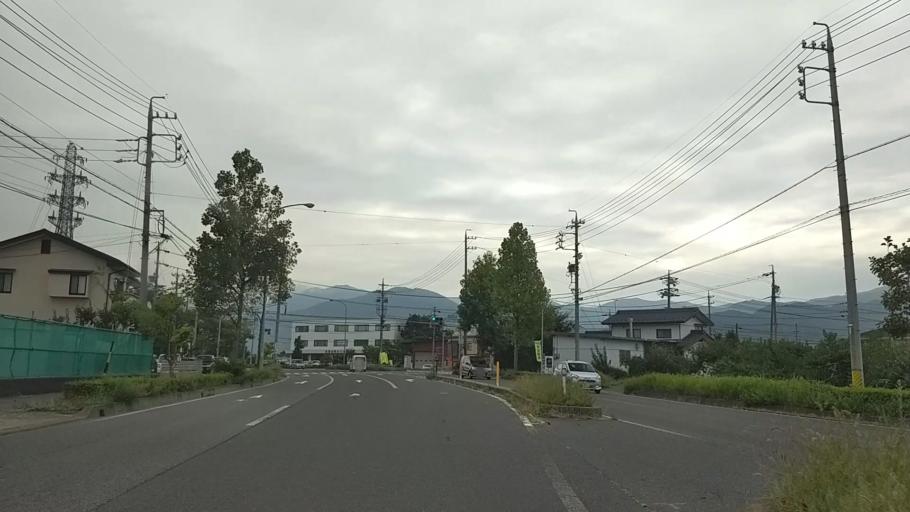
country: JP
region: Nagano
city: Nagano-shi
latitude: 36.6126
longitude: 138.2080
